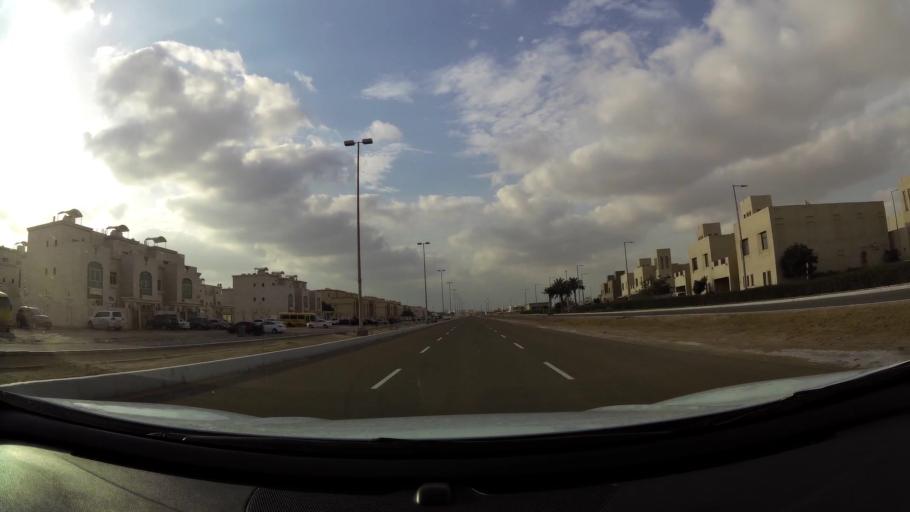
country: AE
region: Abu Dhabi
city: Abu Dhabi
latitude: 24.3669
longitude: 54.5565
